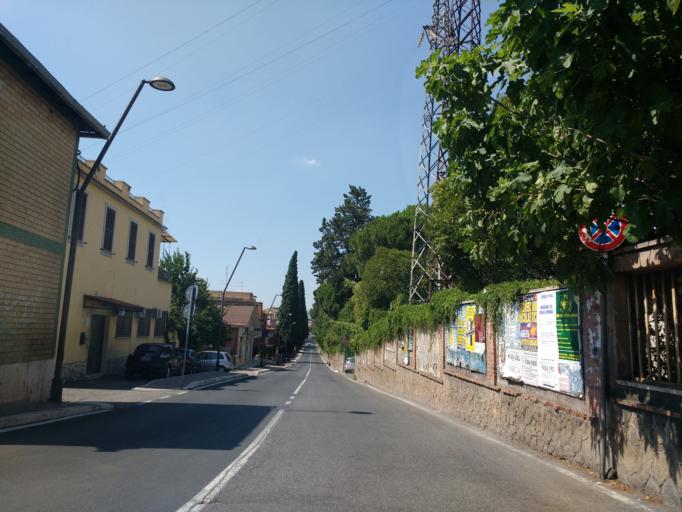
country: IT
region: Latium
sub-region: Citta metropolitana di Roma Capitale
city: Villa Adriana
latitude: 41.9531
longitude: 12.7773
